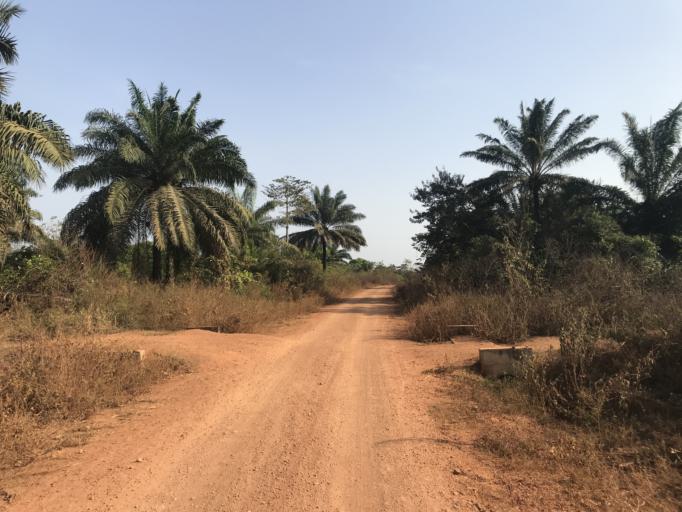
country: NG
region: Osun
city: Inisa
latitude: 7.7942
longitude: 4.2953
